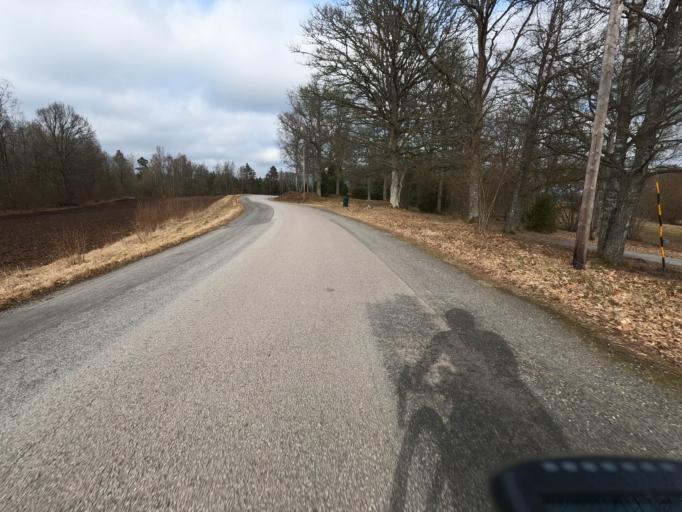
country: SE
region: Kronoberg
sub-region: Alvesta Kommun
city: Alvesta
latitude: 56.8230
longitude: 14.5231
